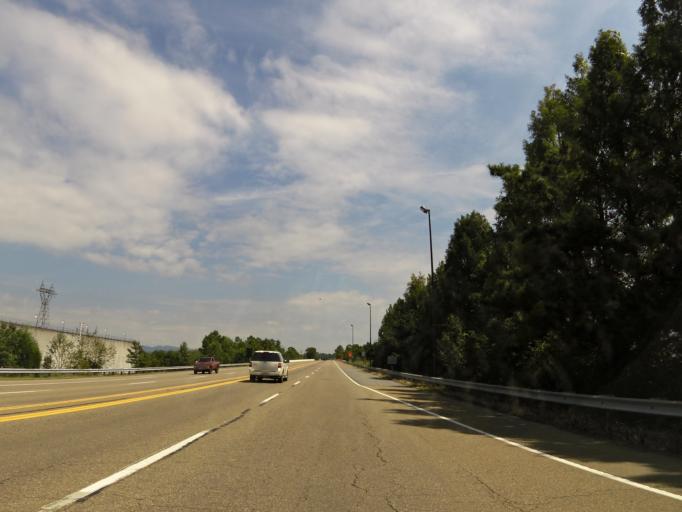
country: US
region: Tennessee
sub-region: Sullivan County
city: Kingsport
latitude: 36.5271
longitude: -82.5571
